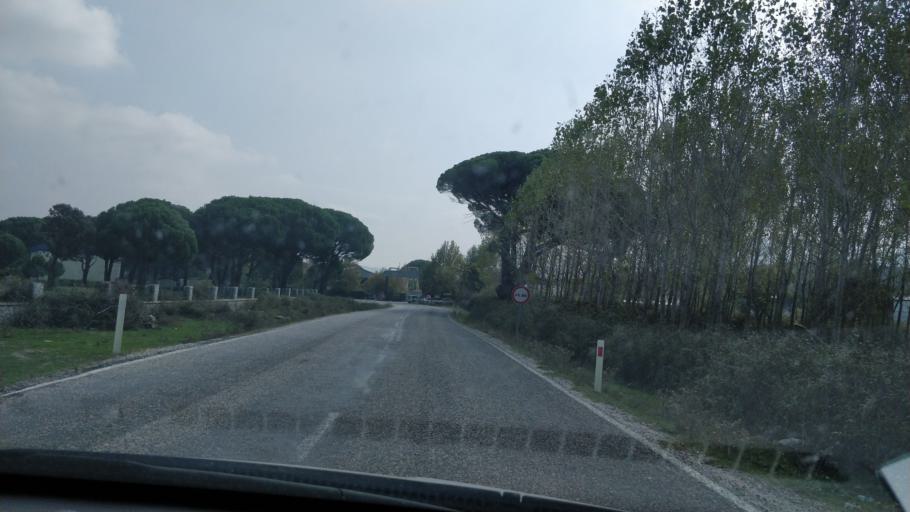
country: TR
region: Izmir
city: Kozak
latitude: 39.2596
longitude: 27.0378
